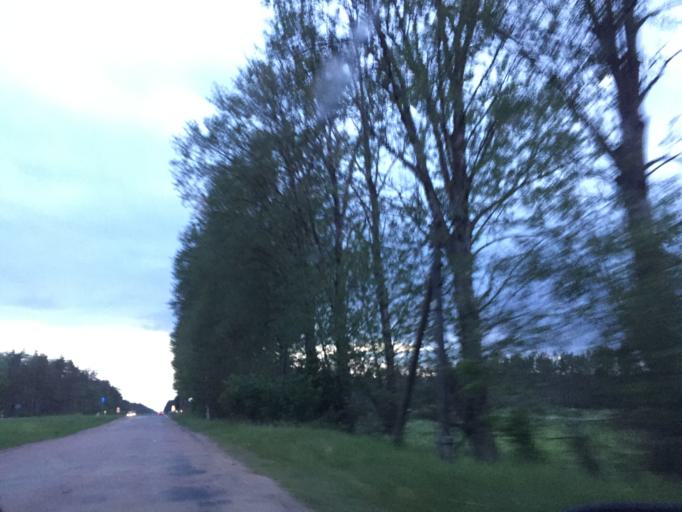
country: LV
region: Garkalne
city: Garkalne
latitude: 57.0392
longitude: 24.3978
